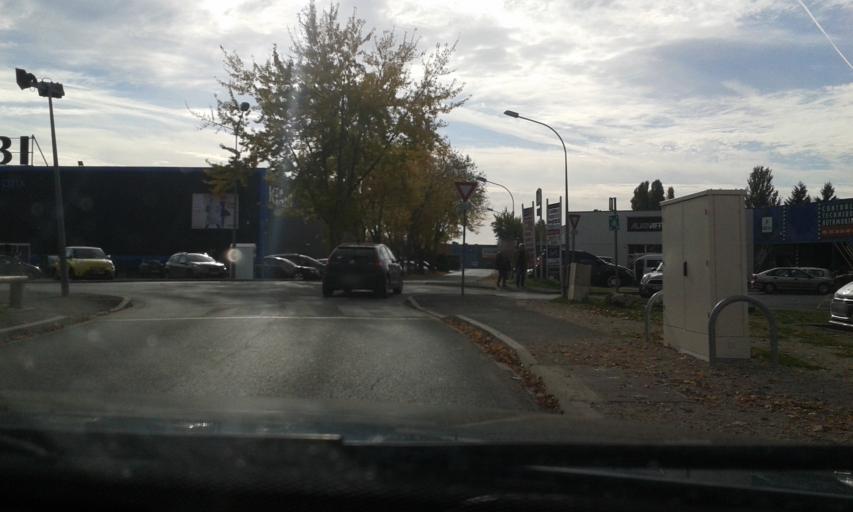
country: FR
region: Centre
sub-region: Departement du Loiret
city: Olivet
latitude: 47.8753
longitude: 1.9113
